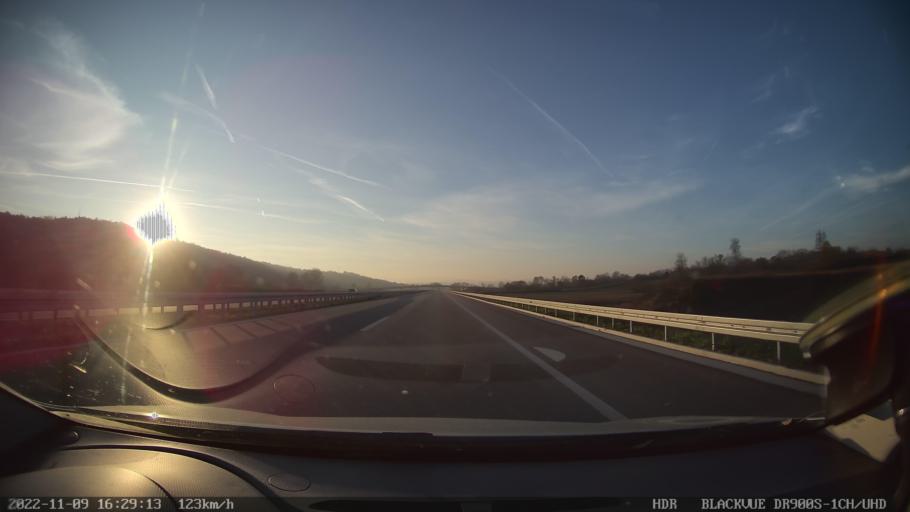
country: RS
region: Central Serbia
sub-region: Moravicki Okrug
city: Cacak
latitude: 43.9236
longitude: 20.3683
